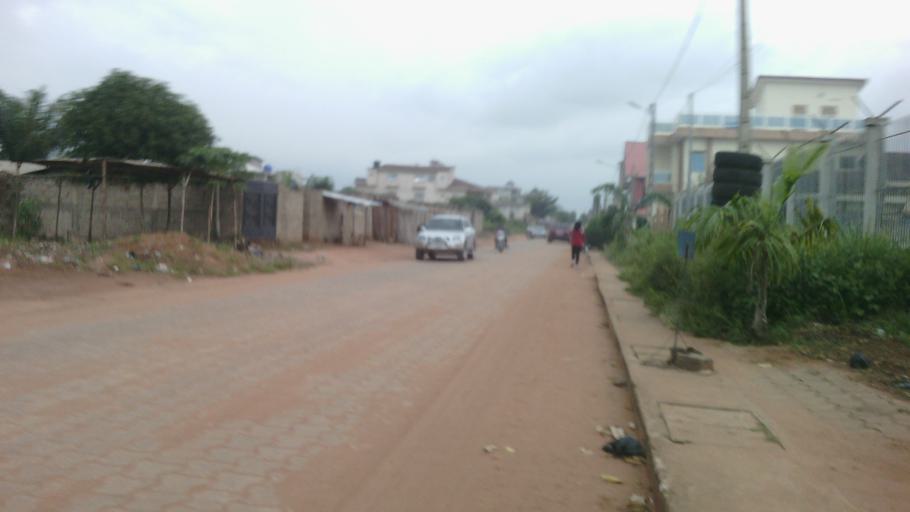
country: BJ
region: Atlantique
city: Abomey-Calavi
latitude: 6.4779
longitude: 2.3476
